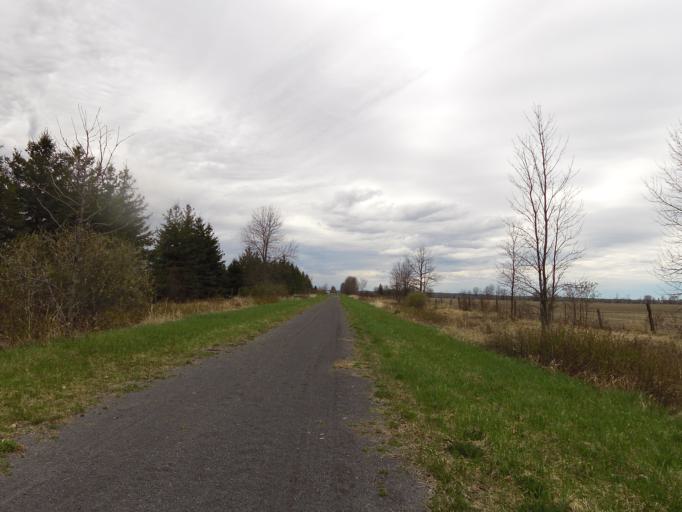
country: CA
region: Ontario
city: Hawkesbury
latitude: 45.5434
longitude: -74.8107
